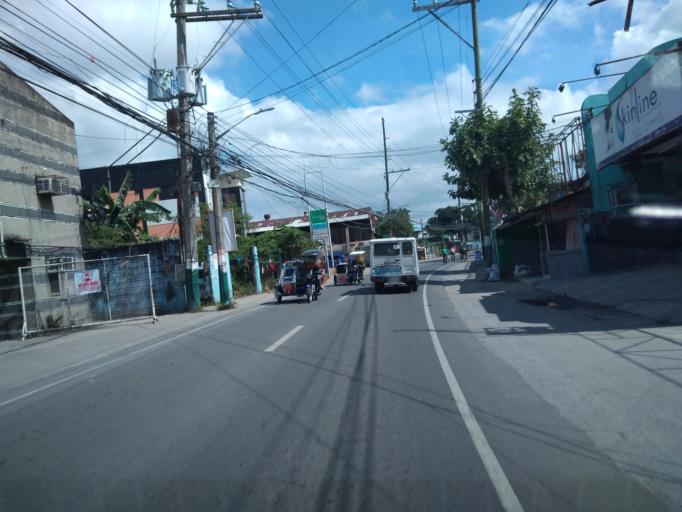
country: PH
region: Central Luzon
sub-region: Province of Bulacan
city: Santa Maria
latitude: 14.8155
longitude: 120.9503
